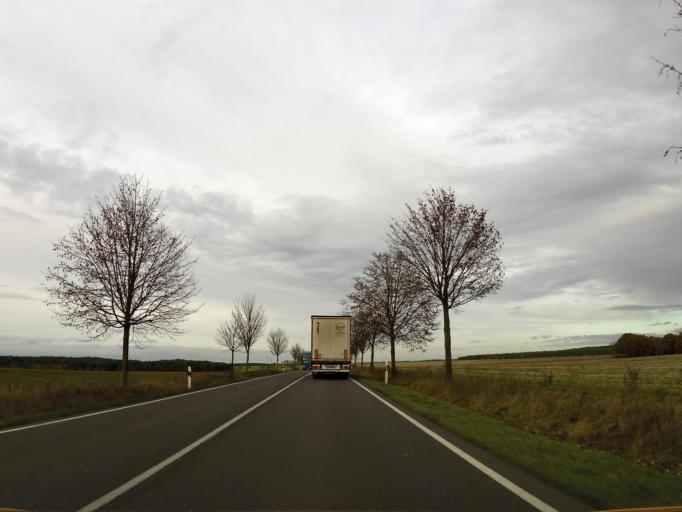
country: DE
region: Saxony-Anhalt
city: Klotze
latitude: 52.7112
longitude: 11.2511
